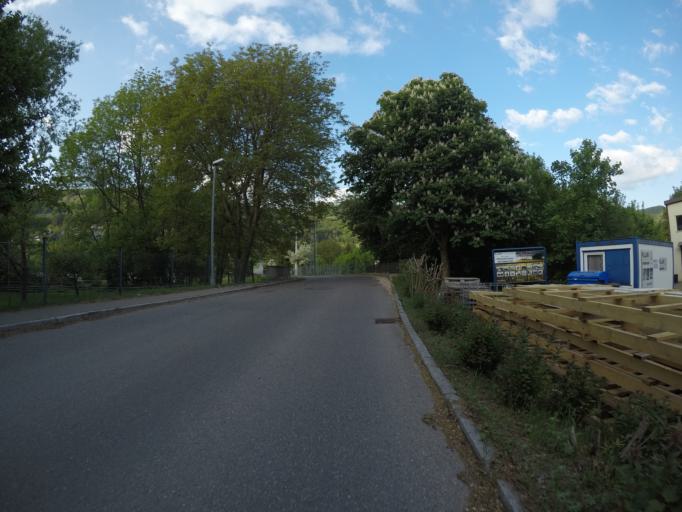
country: DE
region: Baden-Wuerttemberg
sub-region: Tuebingen Region
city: Pfullingen
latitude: 48.4437
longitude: 9.2538
